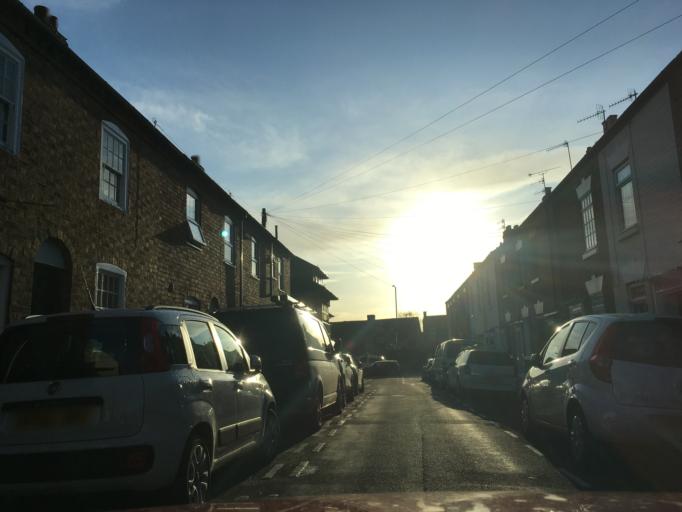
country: GB
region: England
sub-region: Warwickshire
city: Stratford-upon-Avon
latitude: 52.1948
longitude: -1.7072
